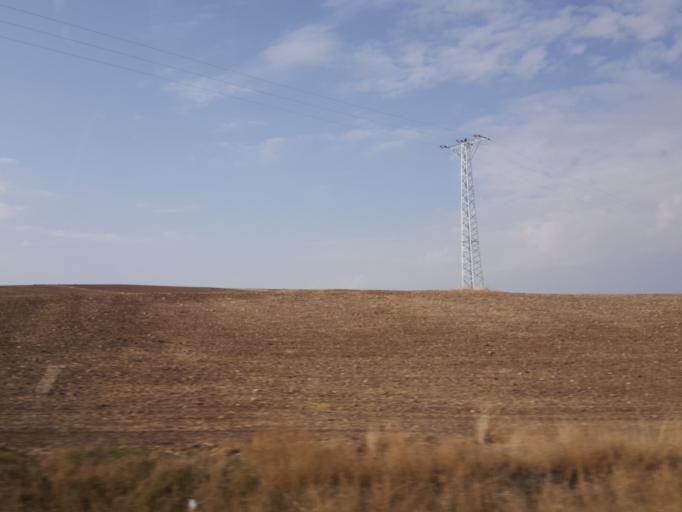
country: TR
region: Corum
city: Cemilbey
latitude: 40.1736
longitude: 35.0448
